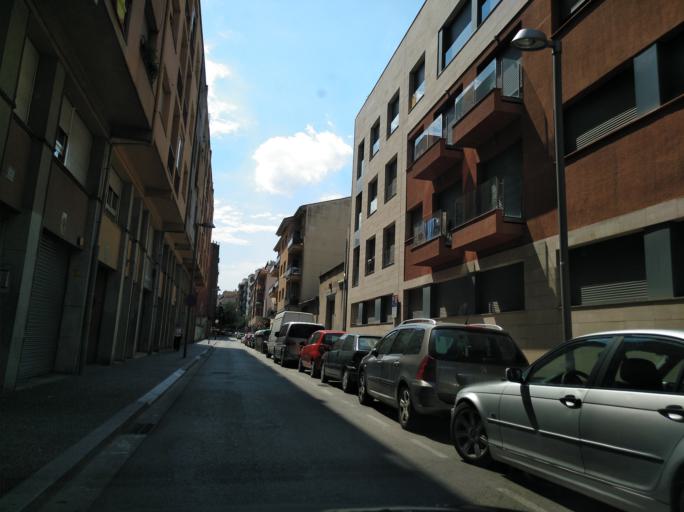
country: ES
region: Catalonia
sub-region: Provincia de Girona
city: Salt
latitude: 41.9770
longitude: 2.8078
